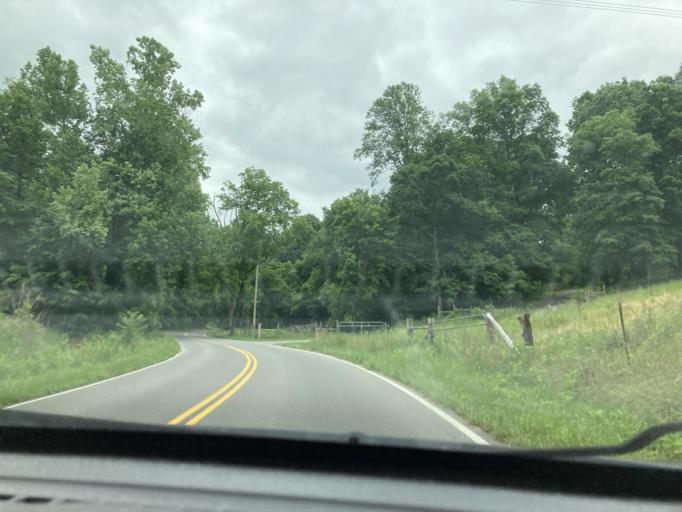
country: US
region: Tennessee
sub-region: Dickson County
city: Dickson
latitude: 36.0393
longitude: -87.3669
